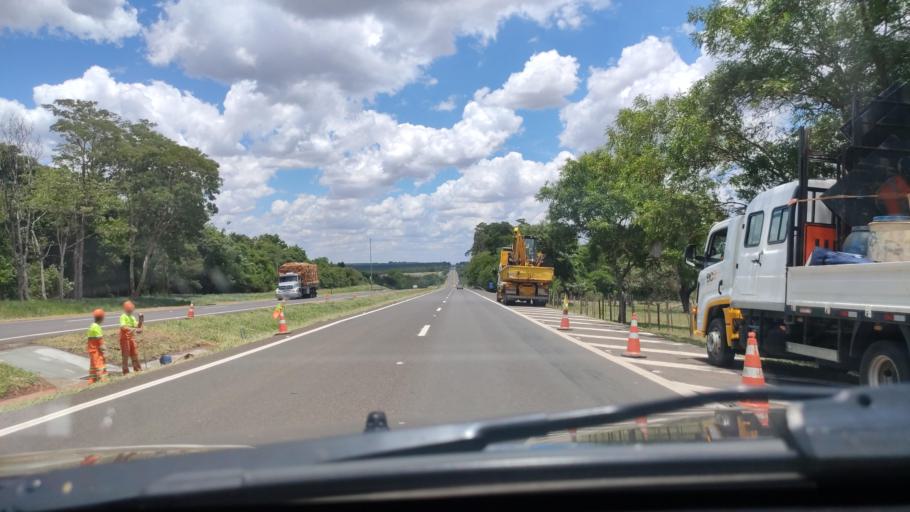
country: BR
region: Sao Paulo
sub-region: Bauru
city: Bauru
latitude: -22.3307
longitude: -48.9183
